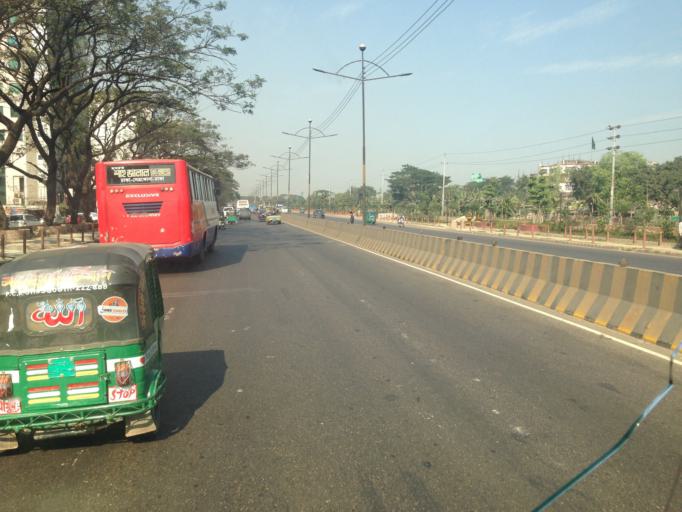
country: BD
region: Dhaka
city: Tungi
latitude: 23.8319
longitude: 90.4194
